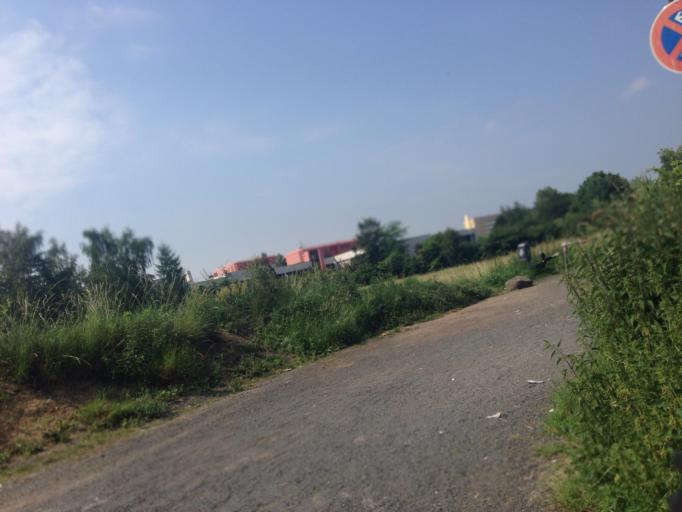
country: DE
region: Hesse
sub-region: Regierungsbezirk Darmstadt
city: Hanau am Main
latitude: 50.1470
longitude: 8.9195
